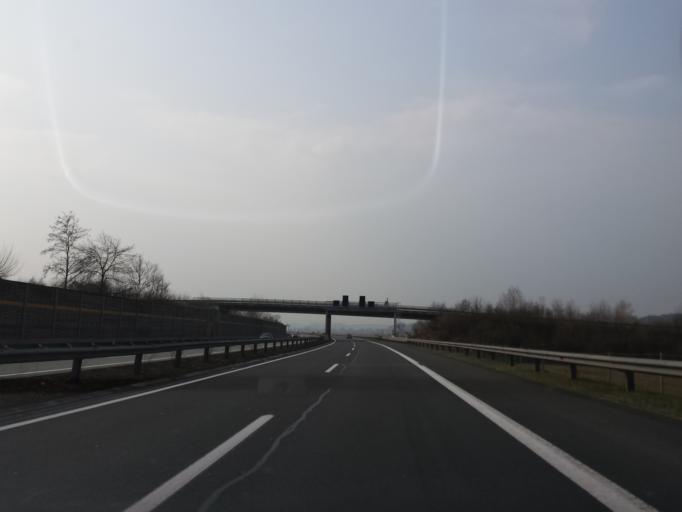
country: AT
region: Styria
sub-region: Politischer Bezirk Hartberg-Fuerstenfeld
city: Nestelbach im Ilztal
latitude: 47.0870
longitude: 15.8712
